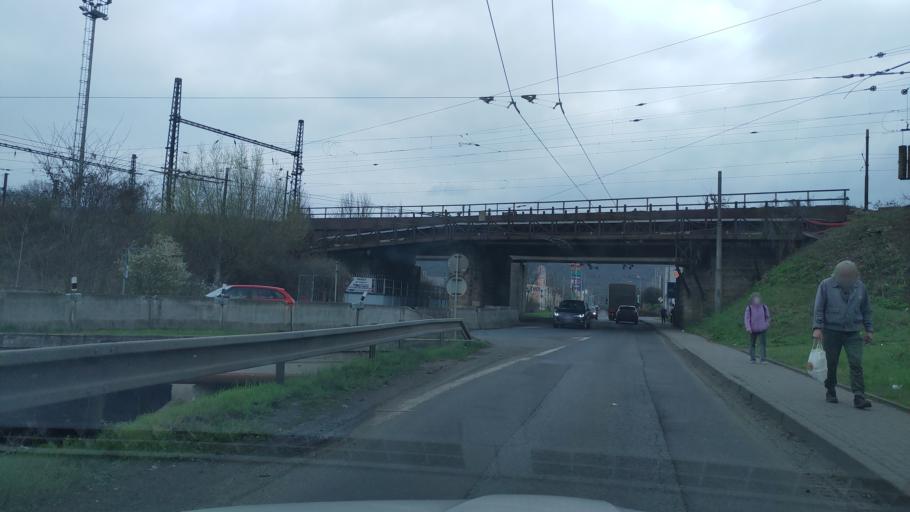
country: CZ
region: Ustecky
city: Trmice
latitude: 50.6534
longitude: 14.0012
